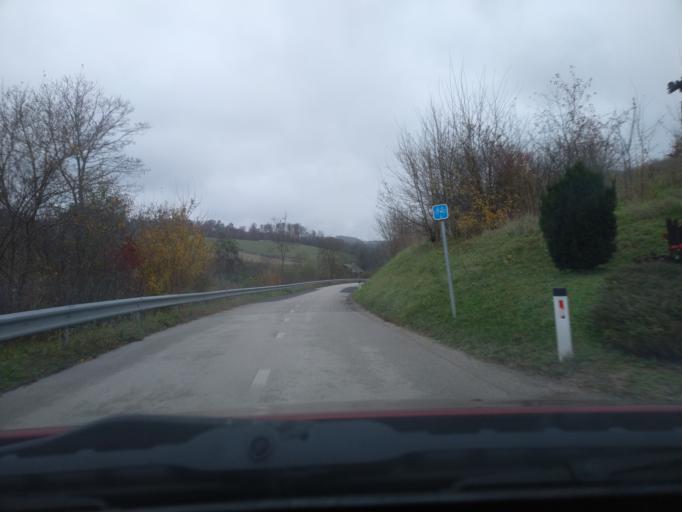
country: SI
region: Kungota
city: Zgornja Kungota
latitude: 46.6655
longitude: 15.6109
